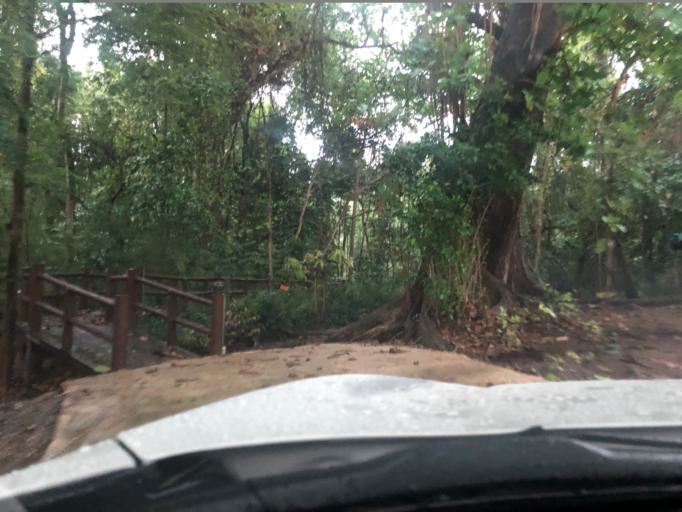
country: TH
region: Lop Buri
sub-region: Amphoe Tha Luang
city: Tha Luang
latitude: 15.0450
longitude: 101.2379
